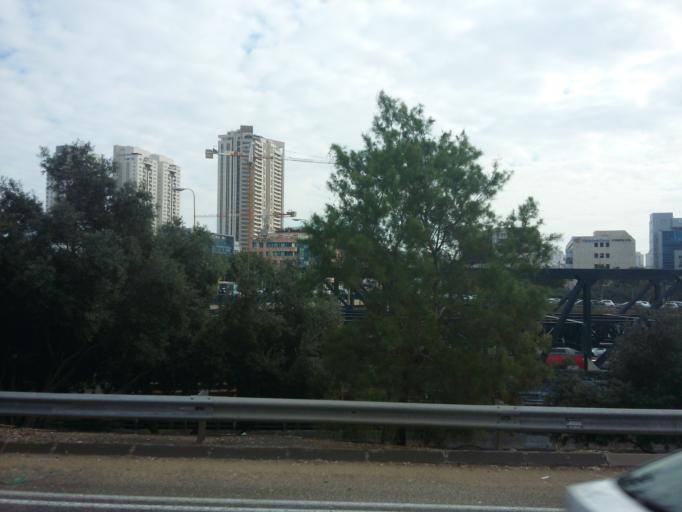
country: IL
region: Tel Aviv
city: Tel Aviv
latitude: 32.0725
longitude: 34.7932
